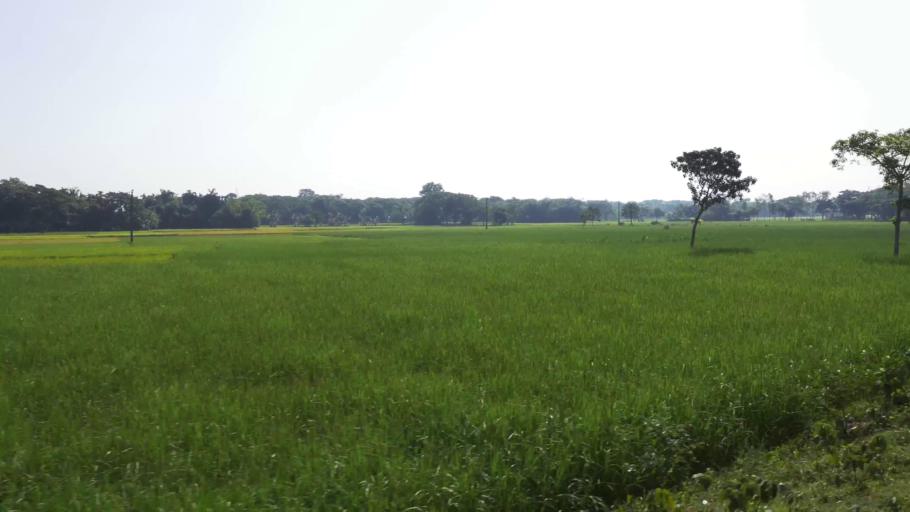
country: BD
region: Dhaka
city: Gafargaon
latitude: 24.5744
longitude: 90.5081
